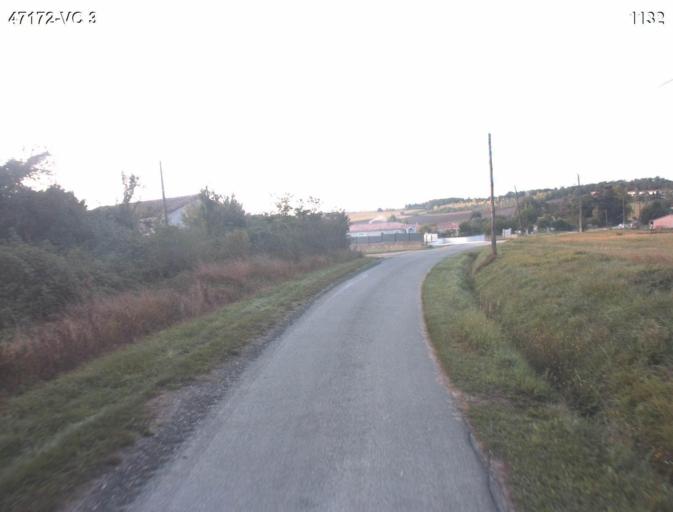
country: FR
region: Aquitaine
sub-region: Departement du Lot-et-Garonne
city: Sainte-Colombe-en-Bruilhois
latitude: 44.1603
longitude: 0.4960
